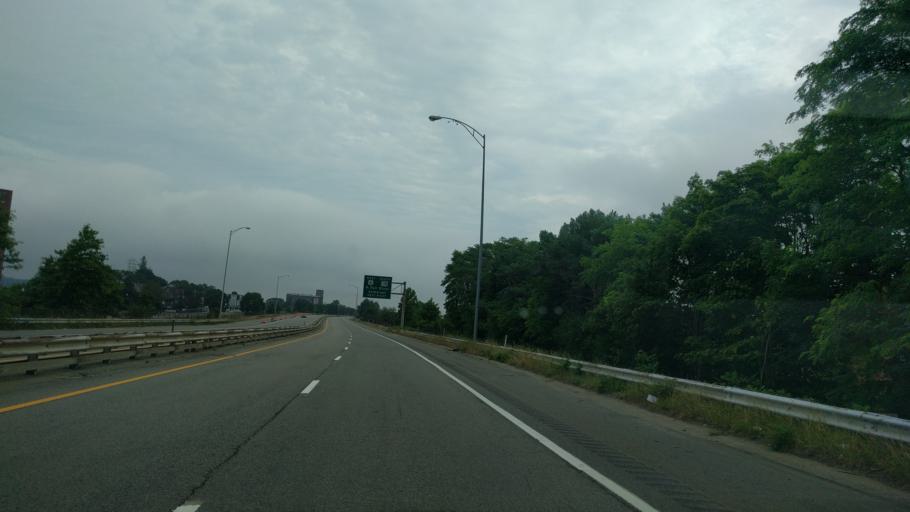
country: US
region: Massachusetts
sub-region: Bristol County
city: Fall River
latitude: 41.7112
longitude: -71.1567
